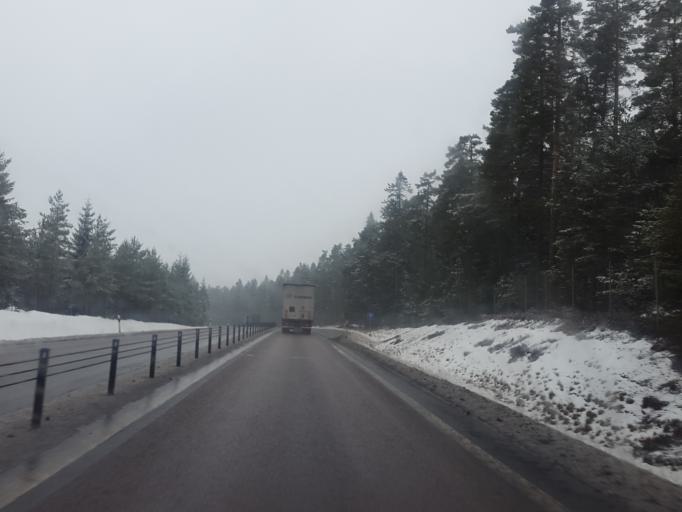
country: SE
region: Joenkoeping
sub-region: Jonkopings Kommun
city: Jonkoping
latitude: 57.7746
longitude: 14.0653
